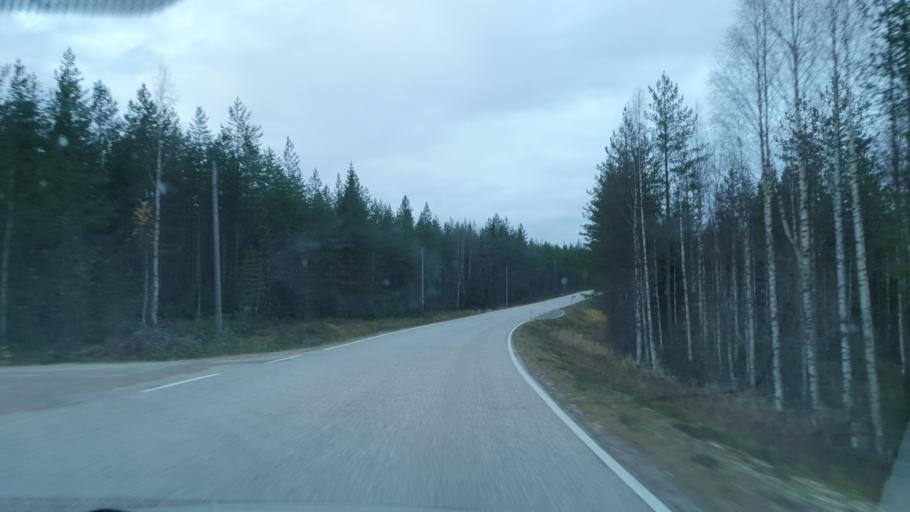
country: FI
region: Kainuu
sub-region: Kajaani
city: Ristijaervi
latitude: 64.4316
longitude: 28.3693
